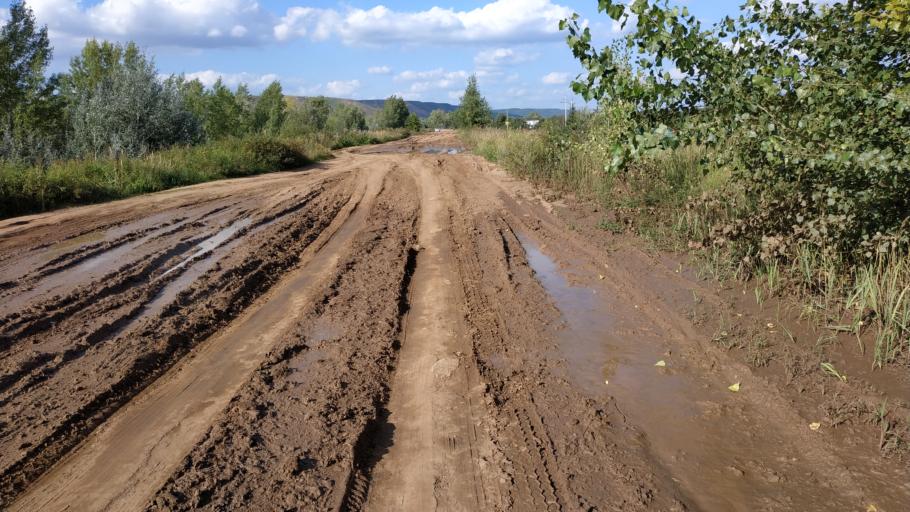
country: RU
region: Tatarstan
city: Nizhnekamsk
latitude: 55.6828
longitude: 51.7304
